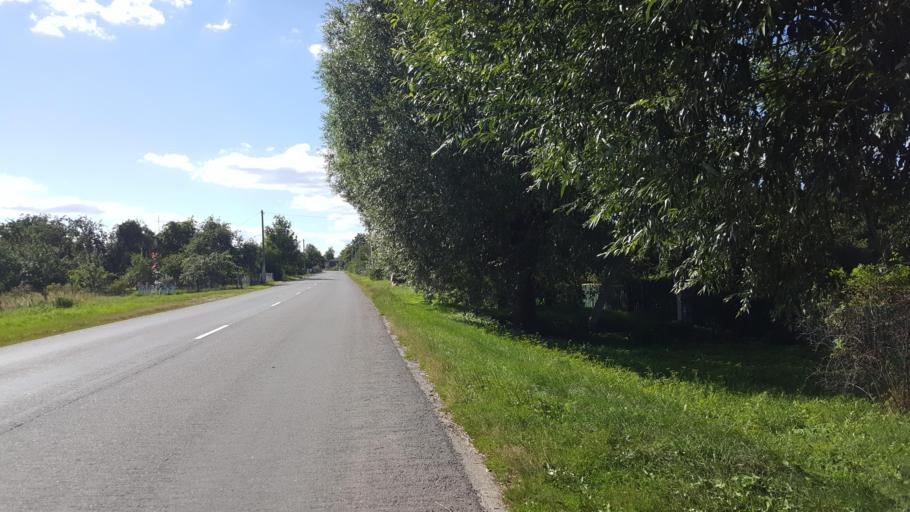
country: BY
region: Brest
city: Kobryn
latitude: 52.3459
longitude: 24.2151
